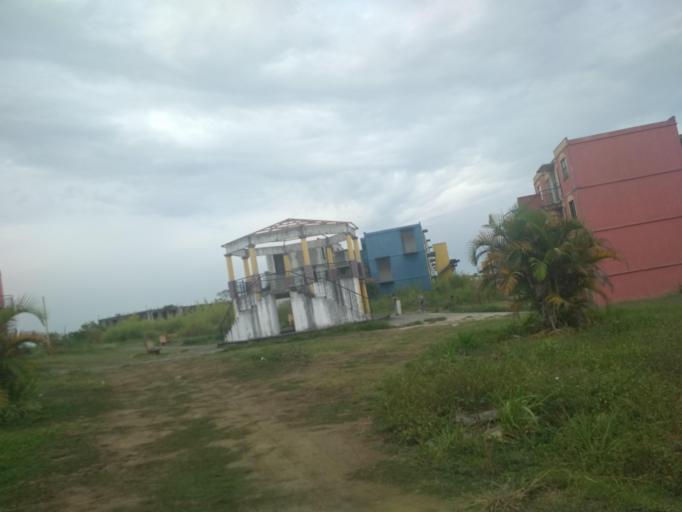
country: MX
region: Veracruz
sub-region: Coatepec
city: Las Lomas
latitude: 19.4171
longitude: -96.9282
